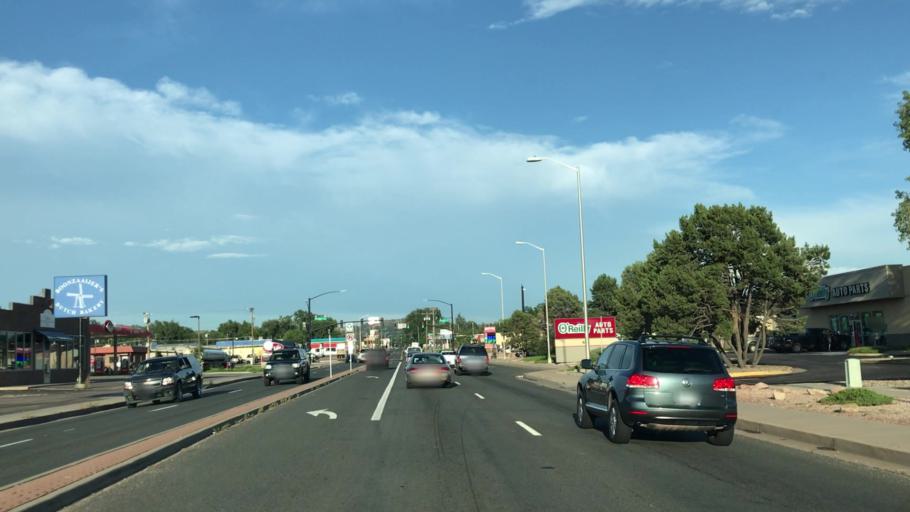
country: US
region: Colorado
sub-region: El Paso County
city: Colorado Springs
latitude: 38.8742
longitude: -104.8146
